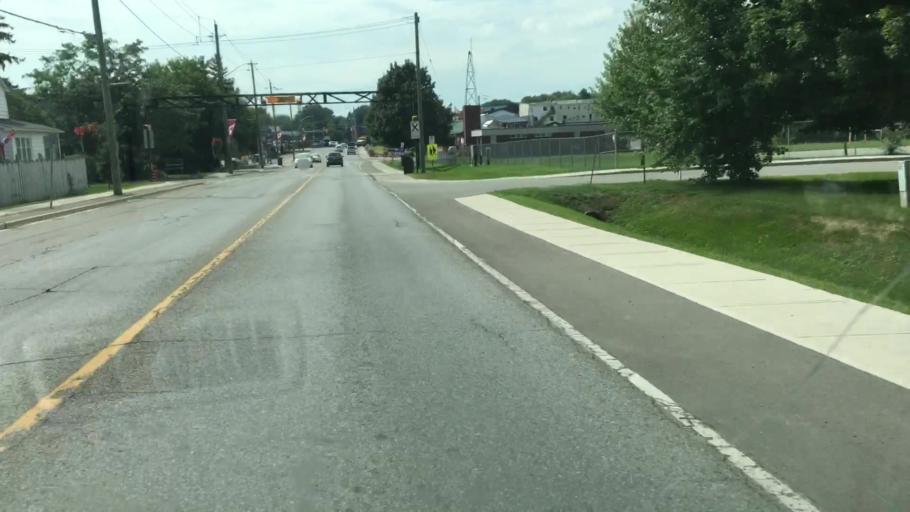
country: CA
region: Ontario
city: Quinte West
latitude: 44.0424
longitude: -77.7334
